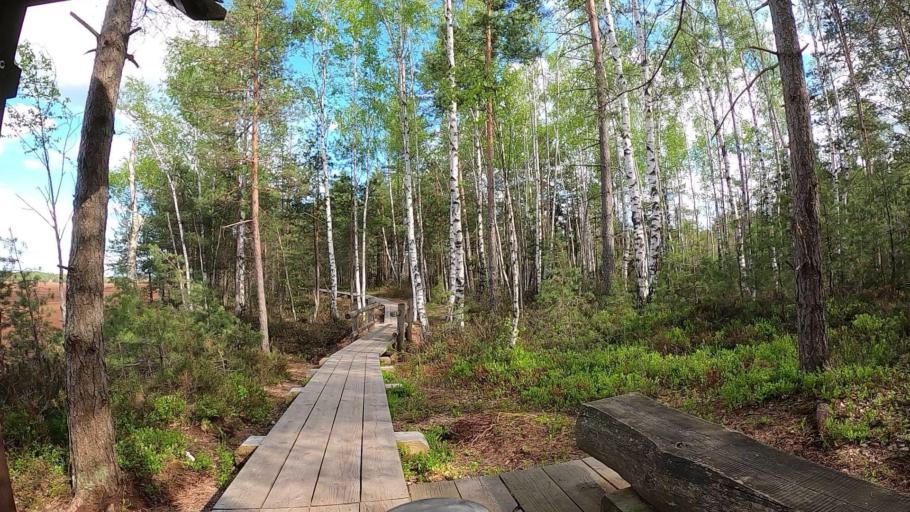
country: LV
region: Jurmala
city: Jurmala
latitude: 56.8593
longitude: 23.7956
